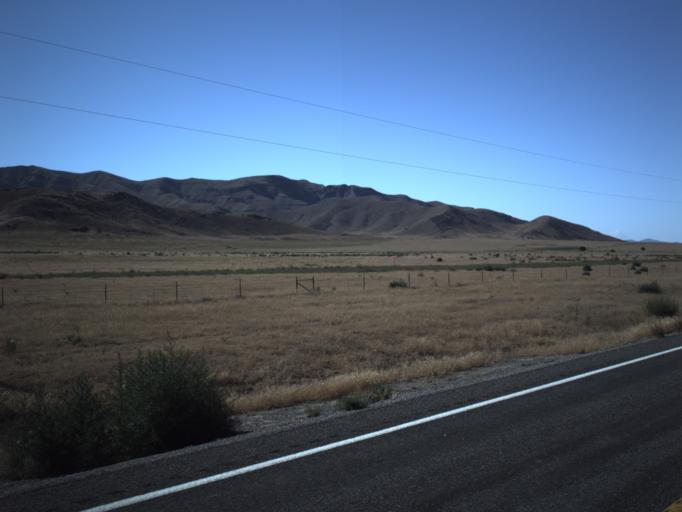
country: US
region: Utah
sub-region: Millard County
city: Delta
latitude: 39.6409
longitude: -112.3043
